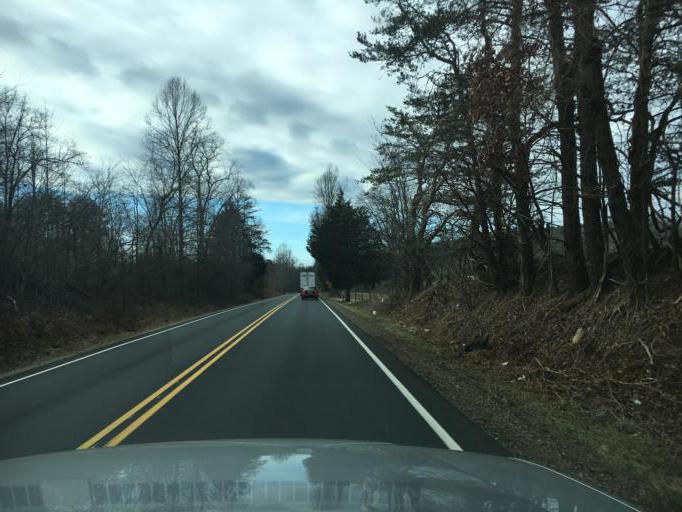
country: US
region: North Carolina
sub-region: Burke County
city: Glen Alpine
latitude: 35.5883
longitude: -81.8336
